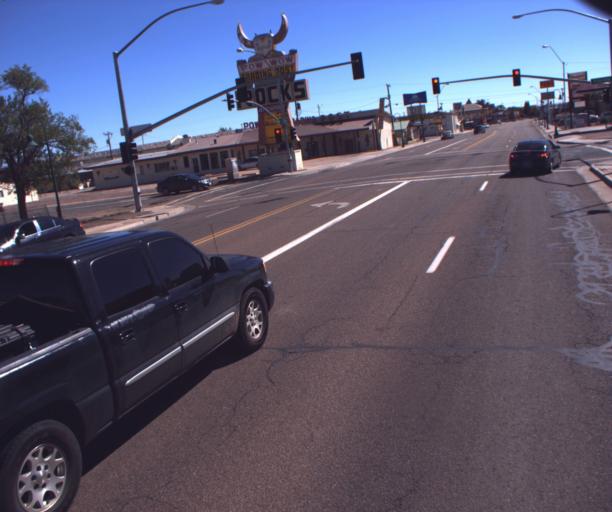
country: US
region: Arizona
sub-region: Navajo County
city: Holbrook
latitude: 34.9074
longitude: -110.1581
